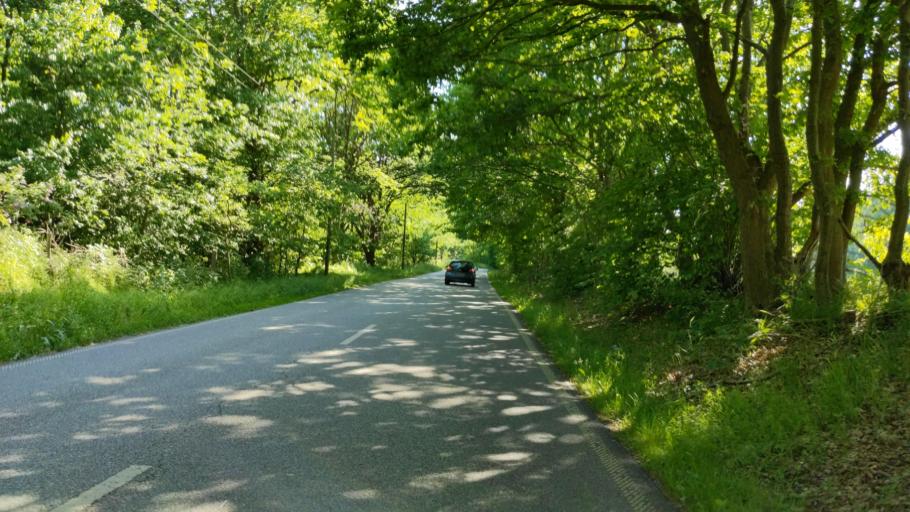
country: DE
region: Schleswig-Holstein
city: Gross Gronau
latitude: 53.7992
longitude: 10.7209
